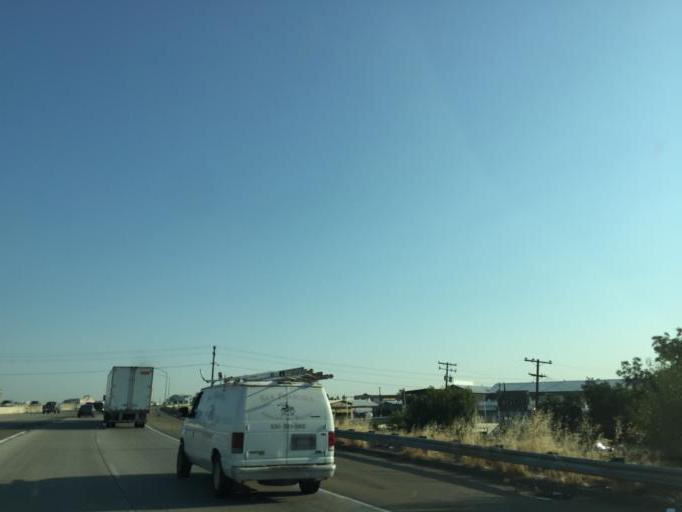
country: US
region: California
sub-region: Fresno County
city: Fresno
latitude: 36.7202
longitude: -119.7850
